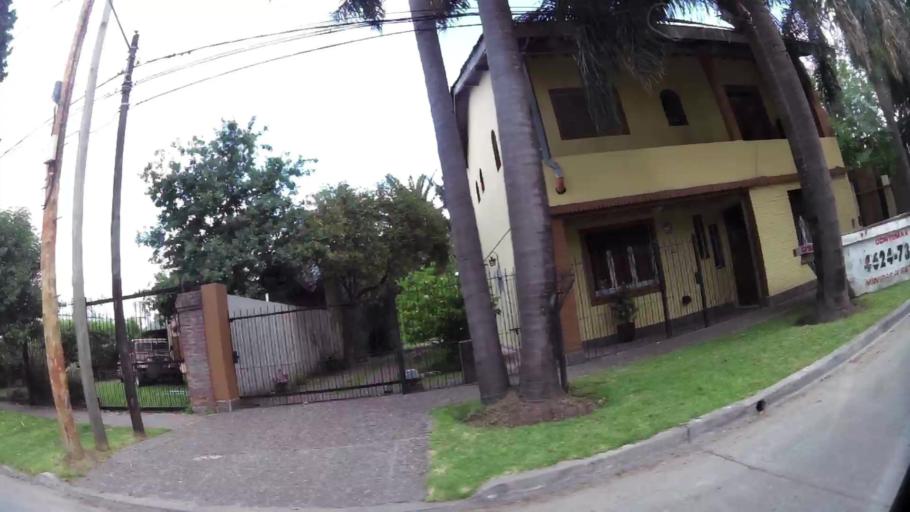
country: AR
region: Buenos Aires
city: Ituzaingo
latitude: -34.6356
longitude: -58.6806
